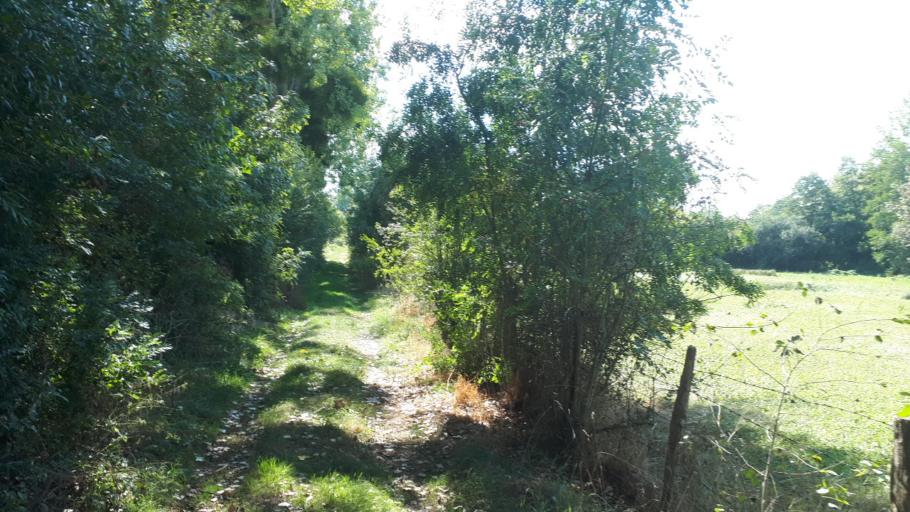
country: FR
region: Centre
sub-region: Departement du Loir-et-Cher
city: Villiers-sur-Loir
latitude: 47.8160
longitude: 0.9595
